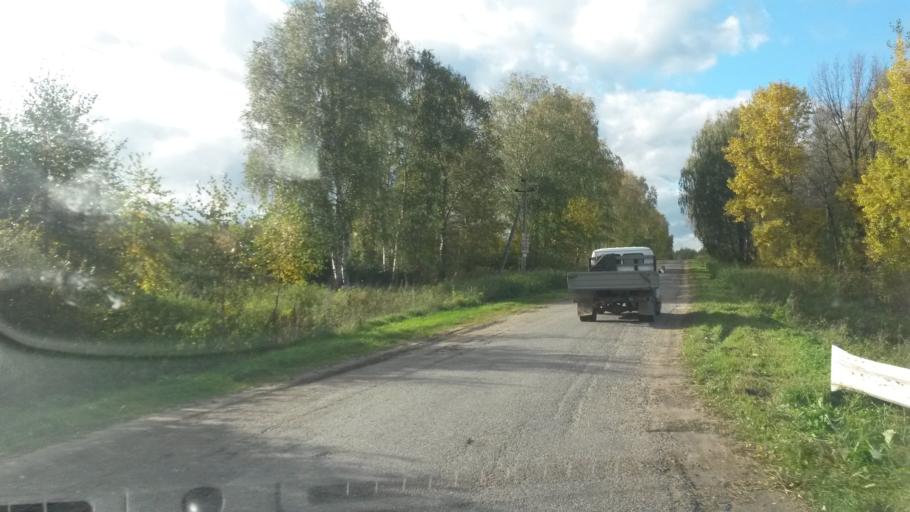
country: RU
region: Jaroslavl
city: Tunoshna
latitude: 57.5243
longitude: 40.0104
